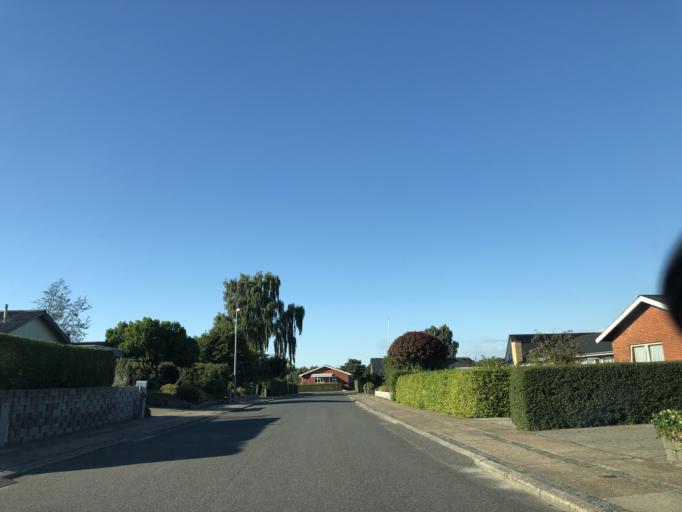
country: DK
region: North Denmark
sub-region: Mariagerfjord Kommune
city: Hobro
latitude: 56.6308
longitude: 9.8044
